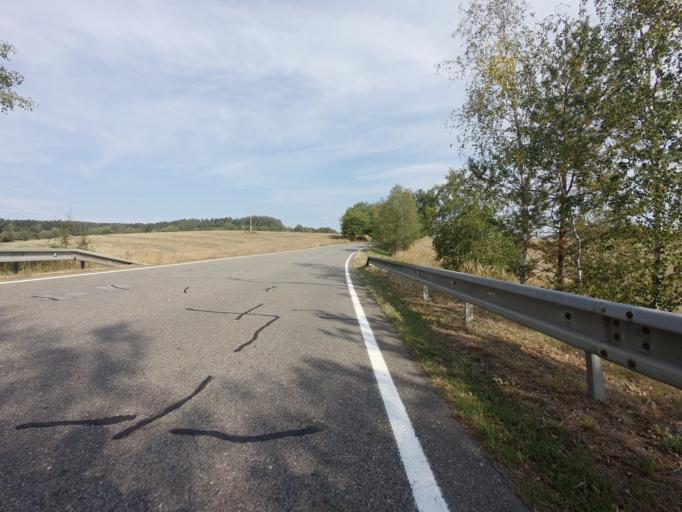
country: CZ
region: Jihocesky
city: Milevsko
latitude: 49.4940
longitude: 14.3618
